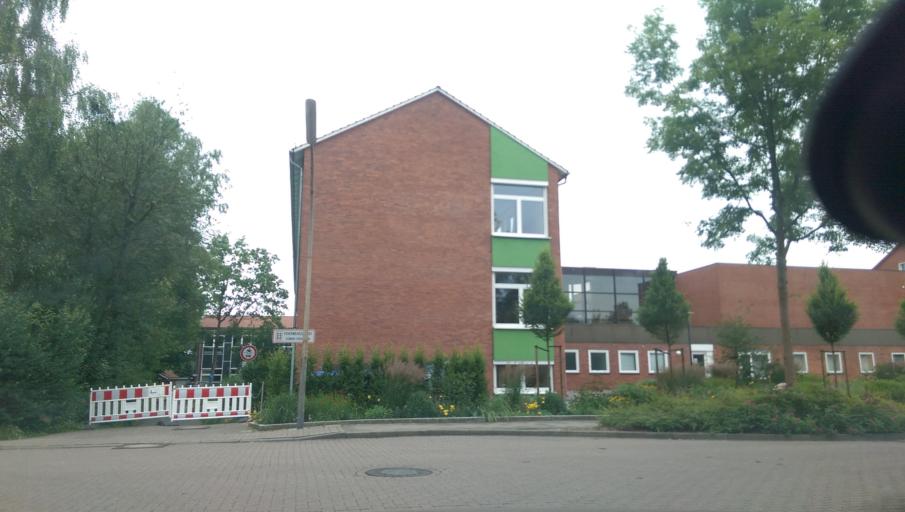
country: DE
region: Lower Saxony
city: Rotenburg
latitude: 53.1036
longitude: 9.3931
